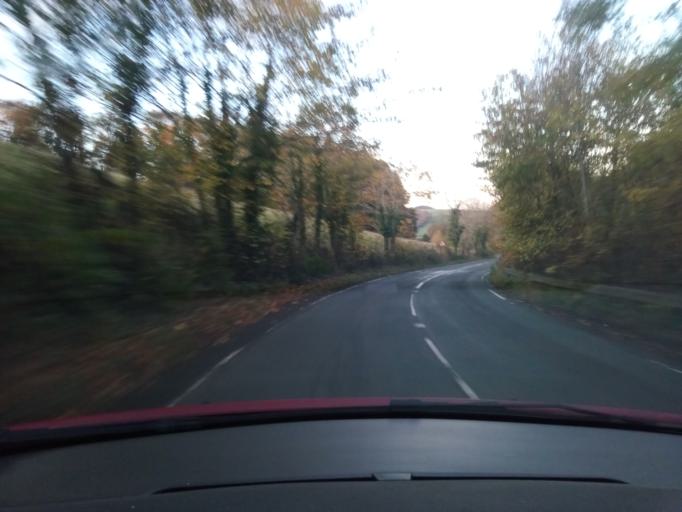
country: GB
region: England
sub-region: Northumberland
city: Bardon Mill
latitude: 54.9647
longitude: -2.2433
